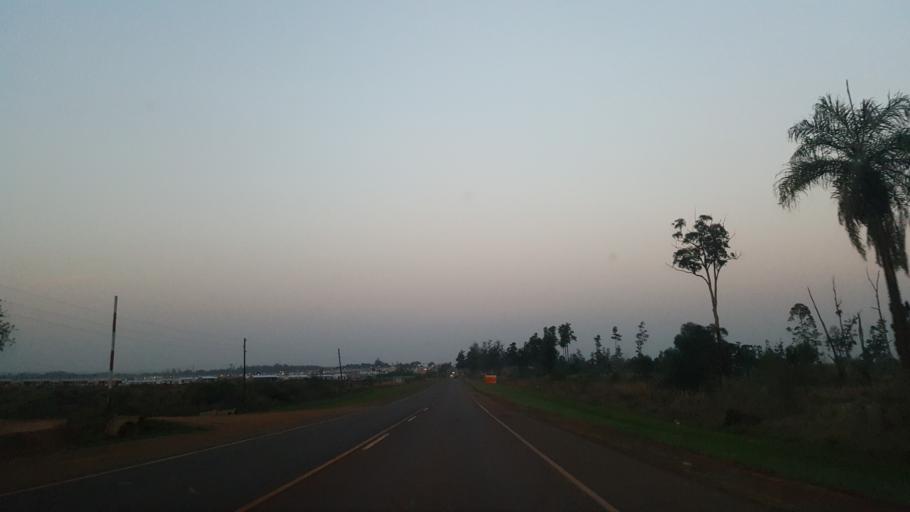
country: AR
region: Misiones
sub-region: Departamento de Capital
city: Posadas
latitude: -27.4200
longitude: -55.9919
